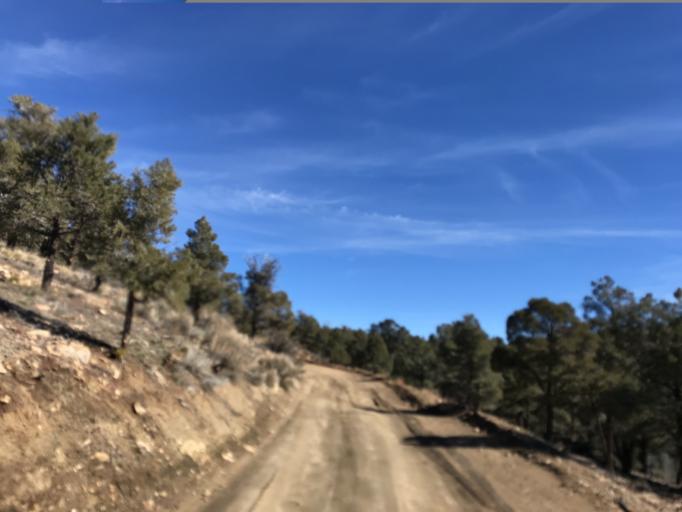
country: US
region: California
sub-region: San Bernardino County
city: Big Bear City
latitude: 34.2796
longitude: -116.7917
